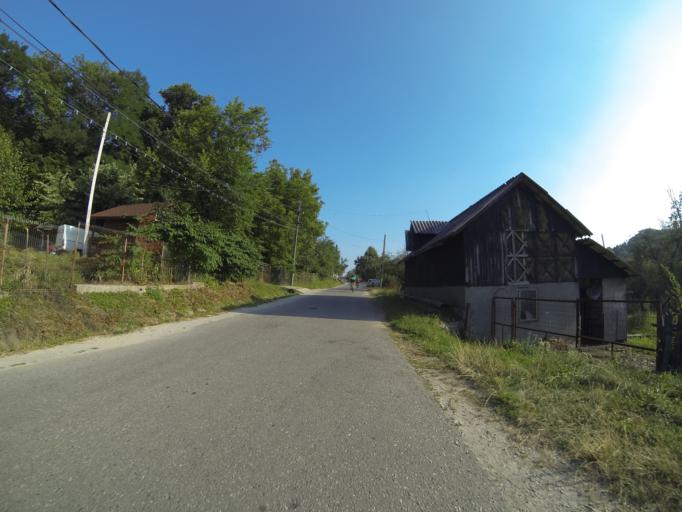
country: RO
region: Valcea
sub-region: Comuna Horezu
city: Horezu
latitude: 45.1681
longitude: 23.9871
